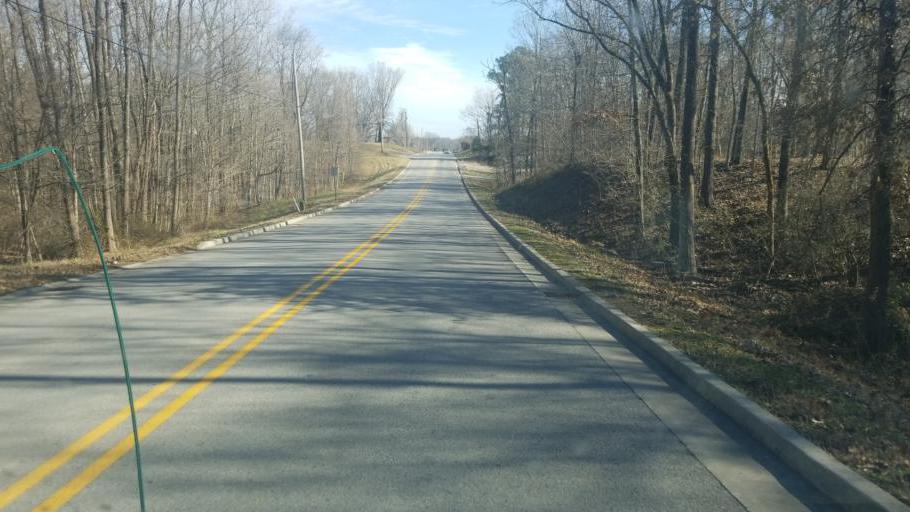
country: US
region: Illinois
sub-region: Jackson County
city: Carbondale
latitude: 37.7006
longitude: -89.1969
